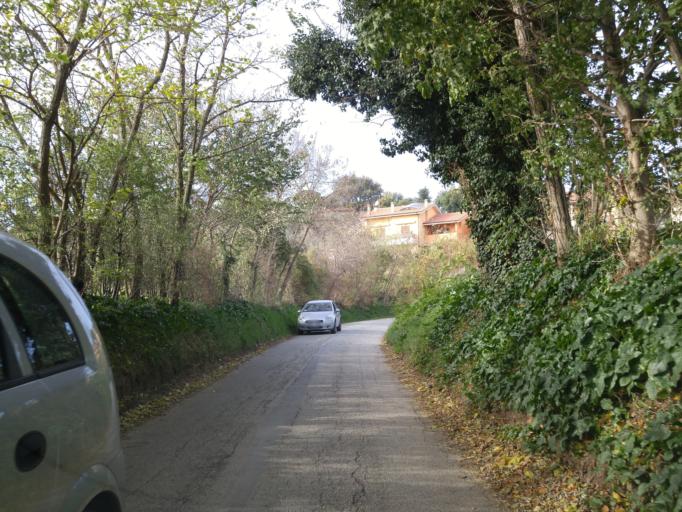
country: IT
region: The Marches
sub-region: Provincia di Pesaro e Urbino
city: Saltara
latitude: 43.7492
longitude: 12.9036
